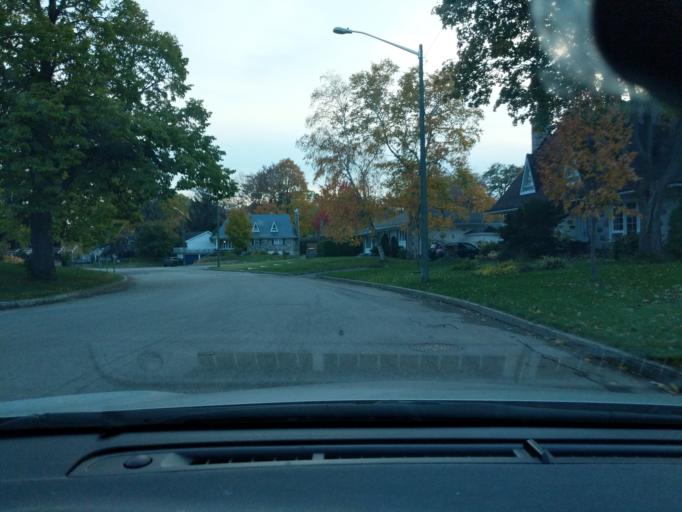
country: CA
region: Quebec
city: Quebec
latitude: 46.7628
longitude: -71.2728
